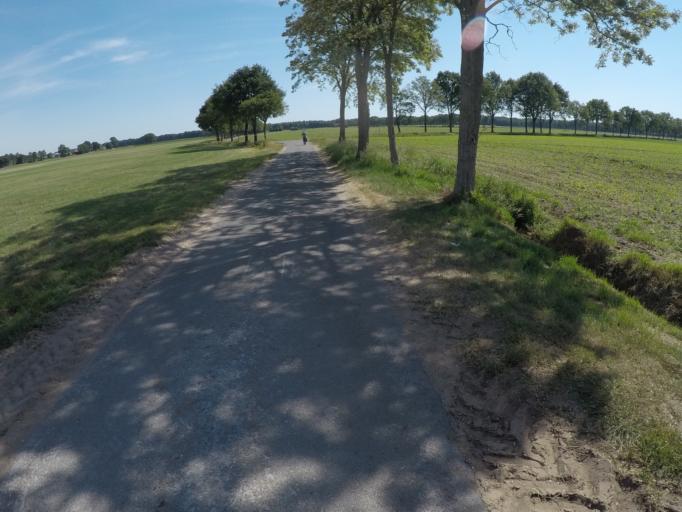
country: BE
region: Flanders
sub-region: Provincie Antwerpen
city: Wuustwezel
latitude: 51.3991
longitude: 4.5381
